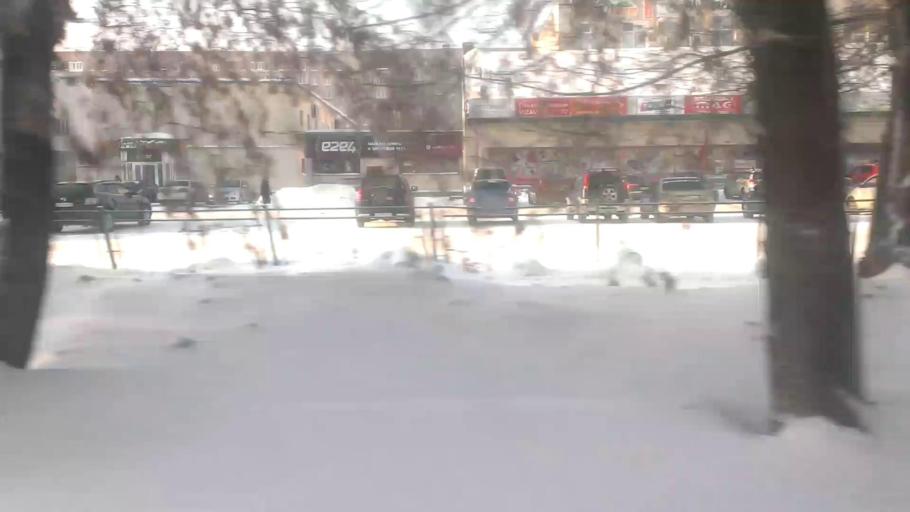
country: RU
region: Altai Krai
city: Novosilikatnyy
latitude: 53.3682
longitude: 83.6766
